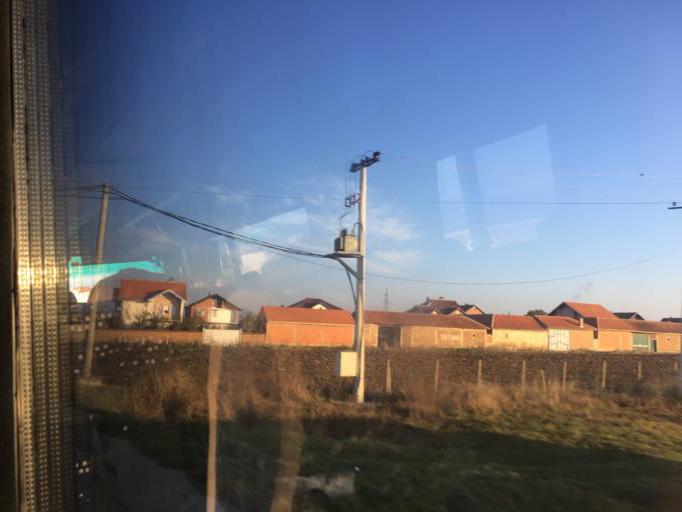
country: XK
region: Pristina
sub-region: Komuna e Drenasit
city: Glogovac
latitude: 42.5845
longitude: 20.8991
